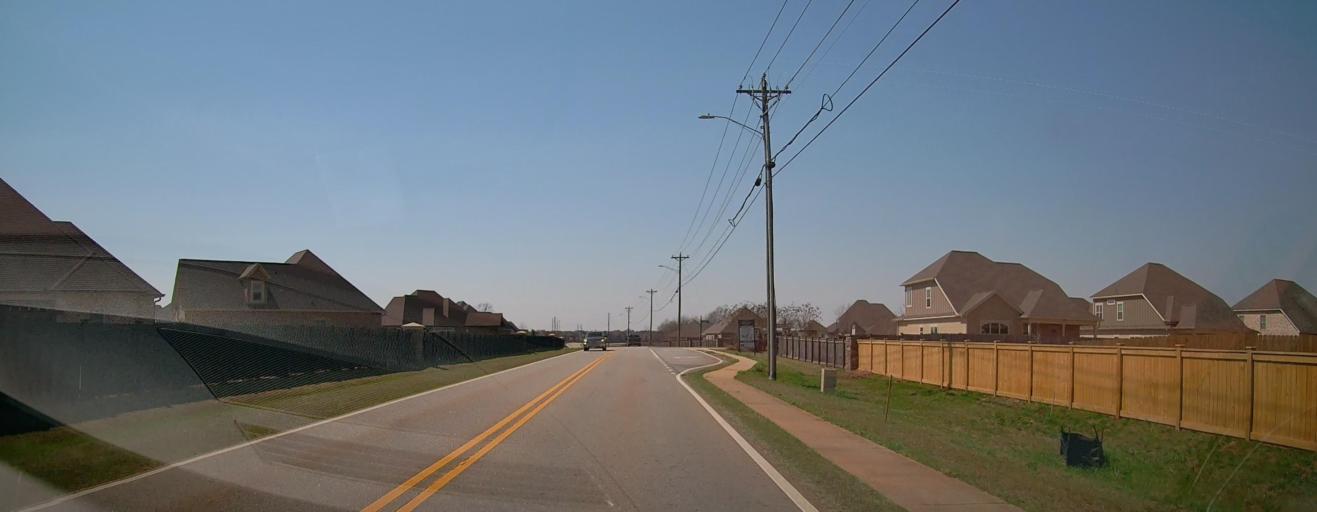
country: US
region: Georgia
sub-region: Houston County
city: Centerville
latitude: 32.5697
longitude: -83.7056
